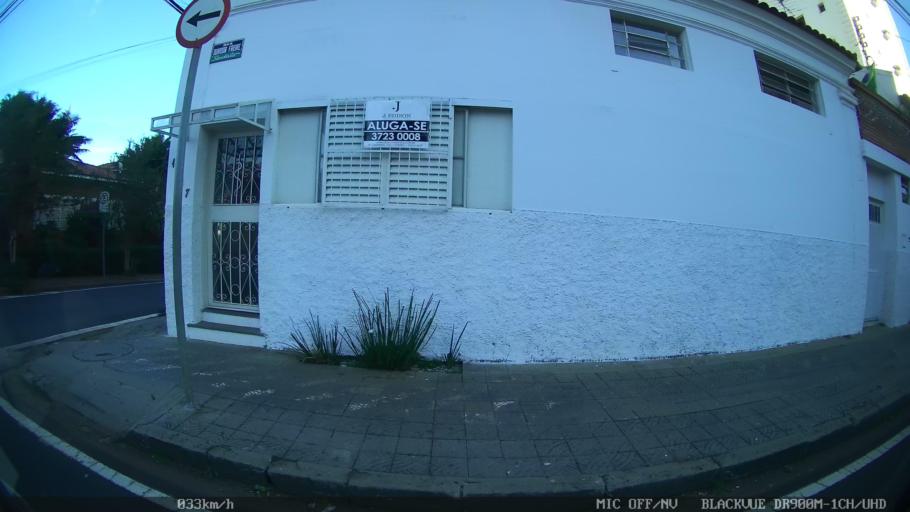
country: BR
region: Sao Paulo
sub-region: Franca
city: Franca
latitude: -20.5407
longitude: -47.4039
